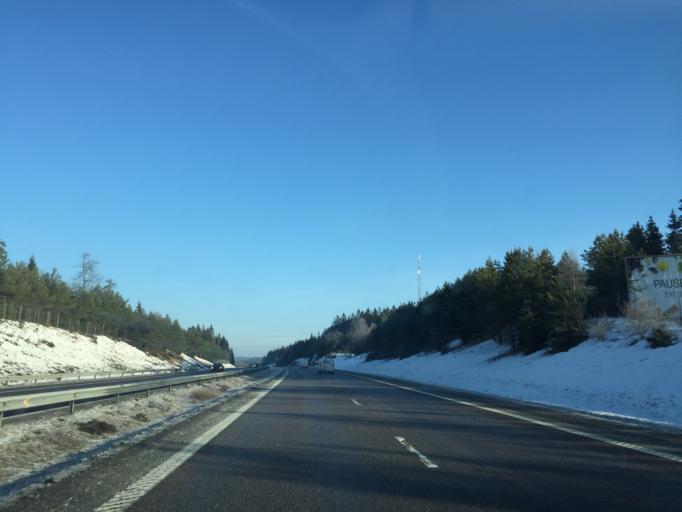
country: SE
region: Vaestra Goetaland
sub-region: Uddevalla Kommun
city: Ljungskile
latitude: 58.1795
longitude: 11.9060
